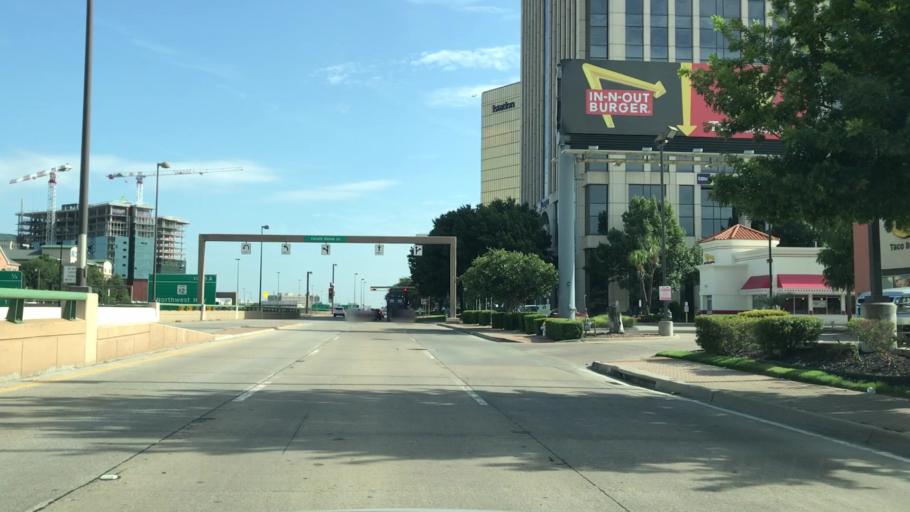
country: US
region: Texas
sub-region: Dallas County
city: University Park
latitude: 32.8593
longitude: -96.7699
